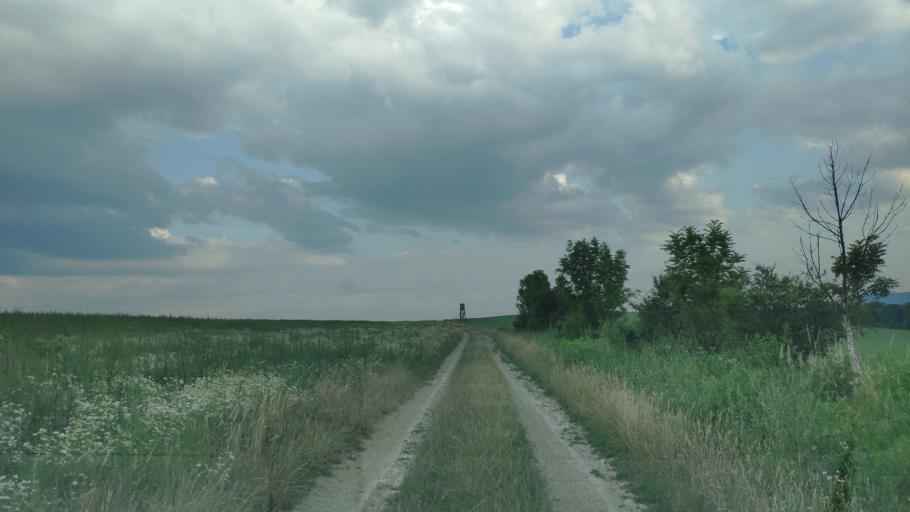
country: SK
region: Kosicky
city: Moldava nad Bodvou
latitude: 48.6941
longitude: 20.9890
